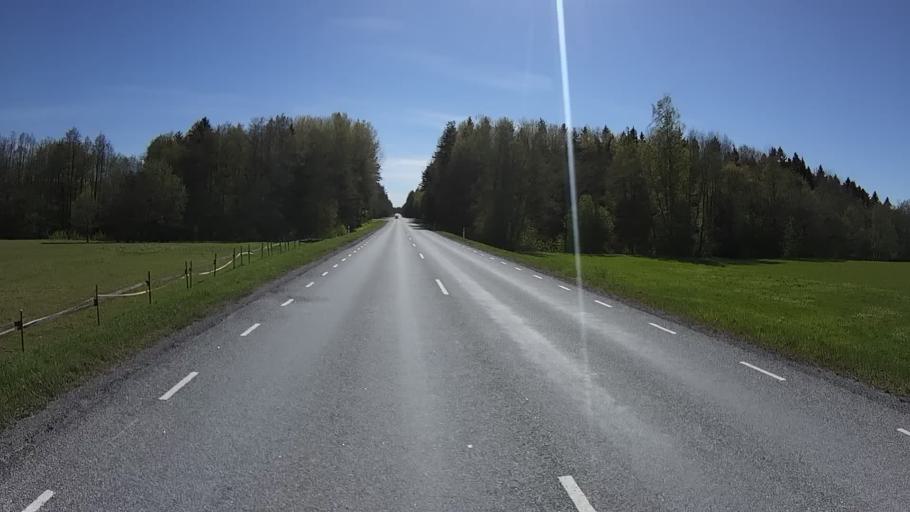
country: EE
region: Harju
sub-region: Loksa linn
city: Loksa
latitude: 59.5190
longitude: 25.6881
